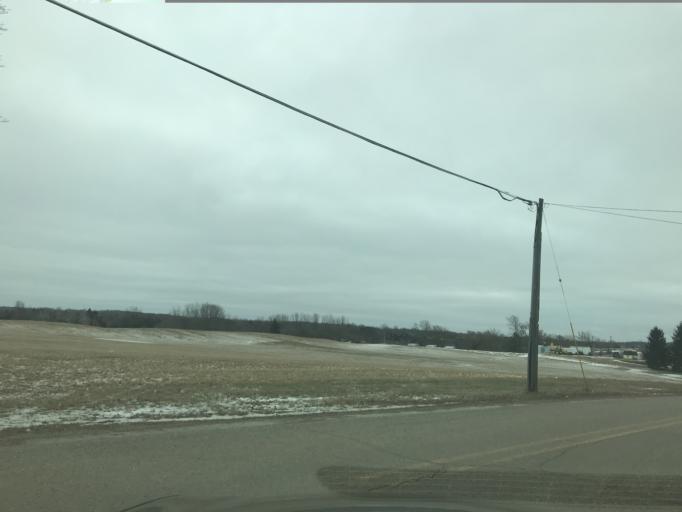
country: US
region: Michigan
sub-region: Jackson County
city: Brooklyn
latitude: 42.0669
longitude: -84.3260
